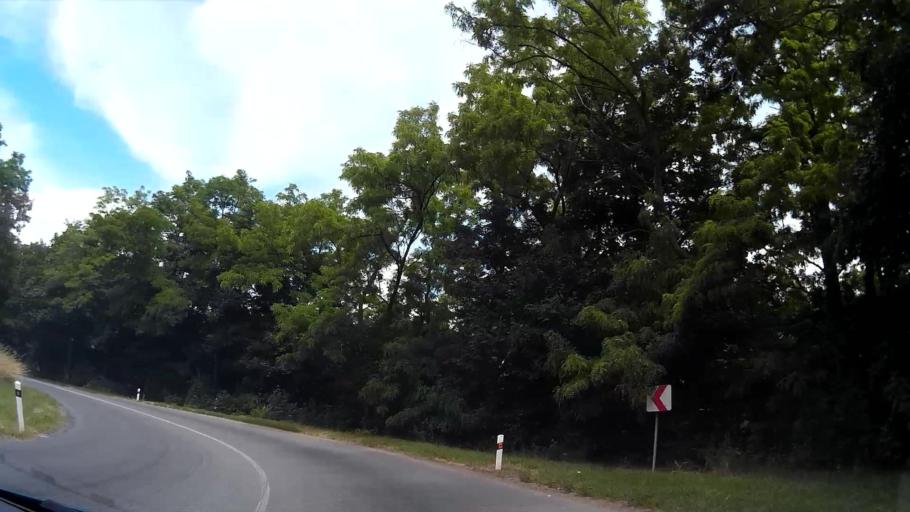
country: CZ
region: South Moravian
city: Ivancice
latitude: 49.0885
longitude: 16.3658
